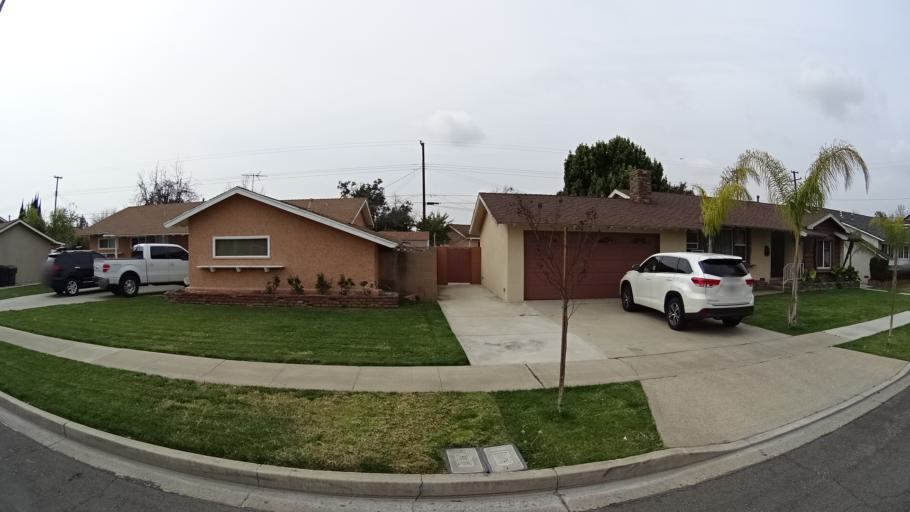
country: US
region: California
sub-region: Orange County
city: Stanton
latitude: 33.8226
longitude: -117.9816
